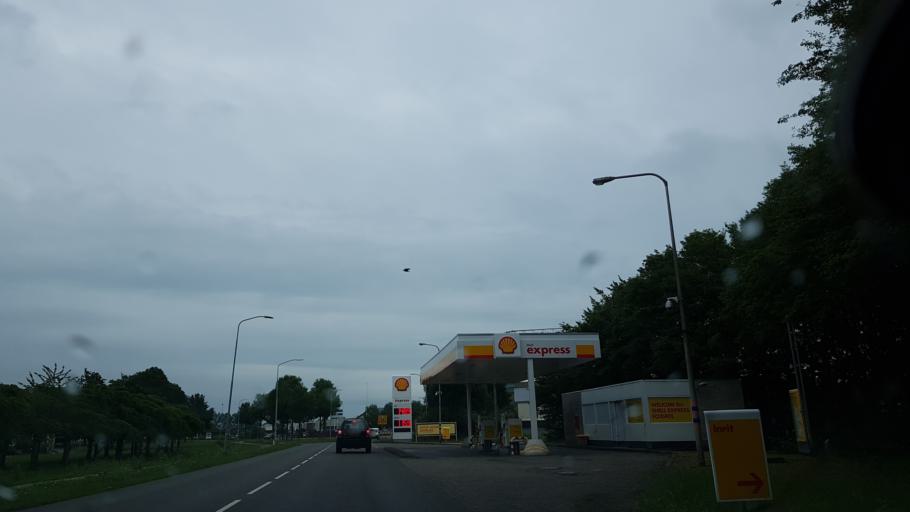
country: NL
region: Groningen
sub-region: Gemeente Hoogezand-Sappemeer
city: Hoogezand
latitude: 53.1670
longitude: 6.7248
